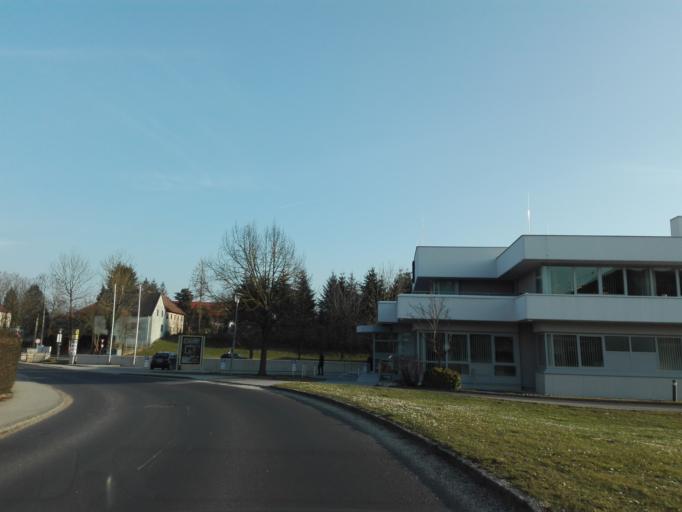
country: AT
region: Upper Austria
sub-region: Politischer Bezirk Linz-Land
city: Horsching
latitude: 48.2269
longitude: 14.1758
